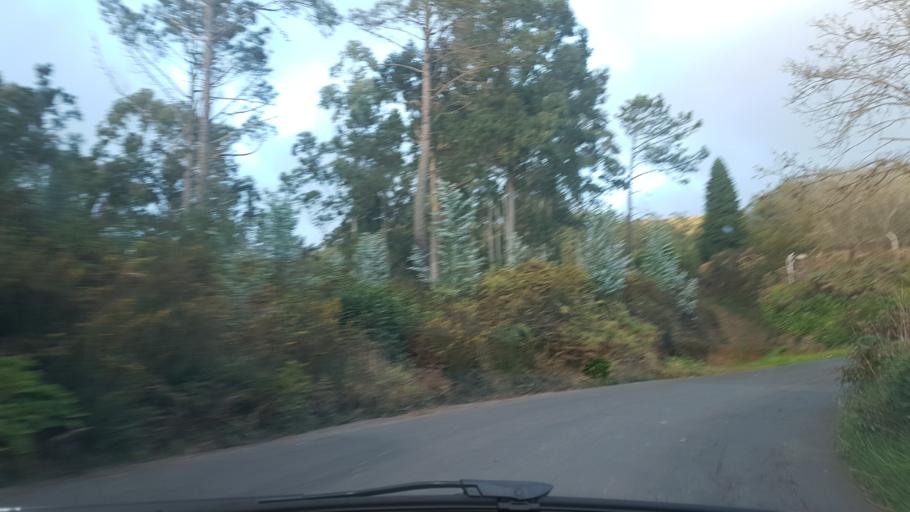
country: PT
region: Madeira
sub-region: Calheta
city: Arco da Calheta
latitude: 32.7258
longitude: -17.1112
